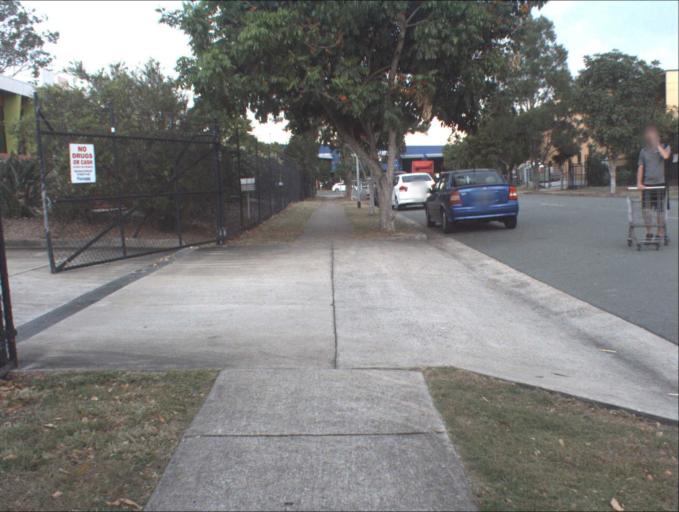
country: AU
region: Queensland
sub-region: Logan
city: Beenleigh
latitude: -27.6853
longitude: 153.1928
